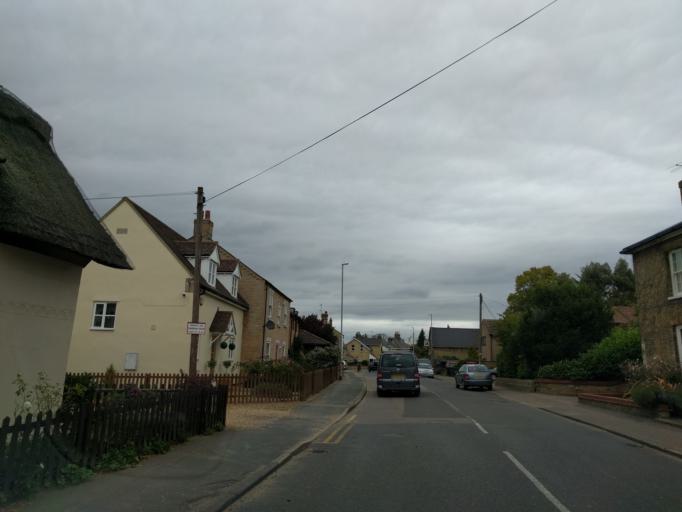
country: GB
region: England
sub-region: Cambridgeshire
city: Earith
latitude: 52.3123
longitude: 0.0563
